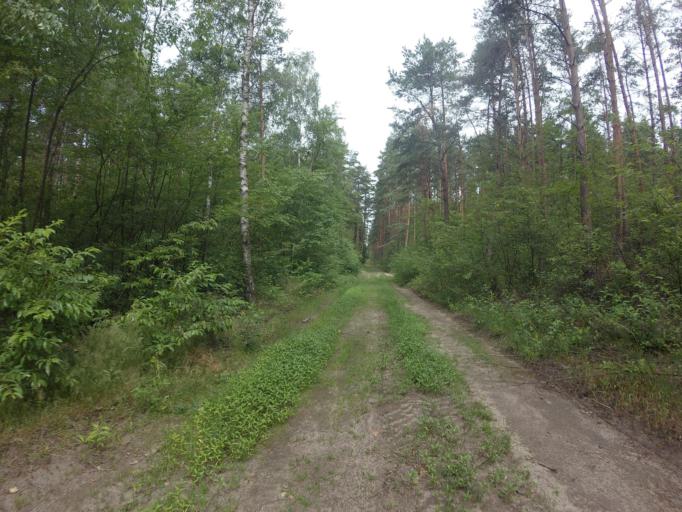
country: PL
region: West Pomeranian Voivodeship
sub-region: Powiat choszczenski
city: Bierzwnik
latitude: 53.1259
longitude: 15.6645
